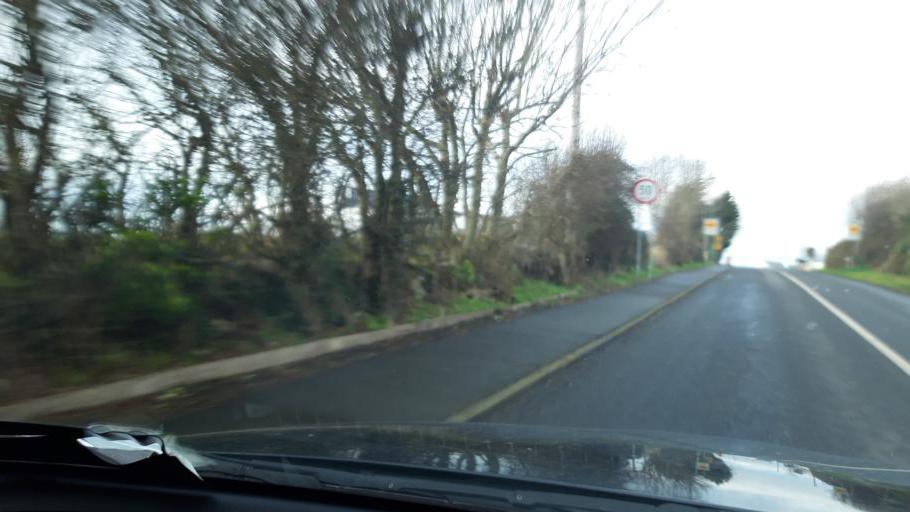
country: IE
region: Leinster
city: An Ros
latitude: 53.5453
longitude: -6.0995
